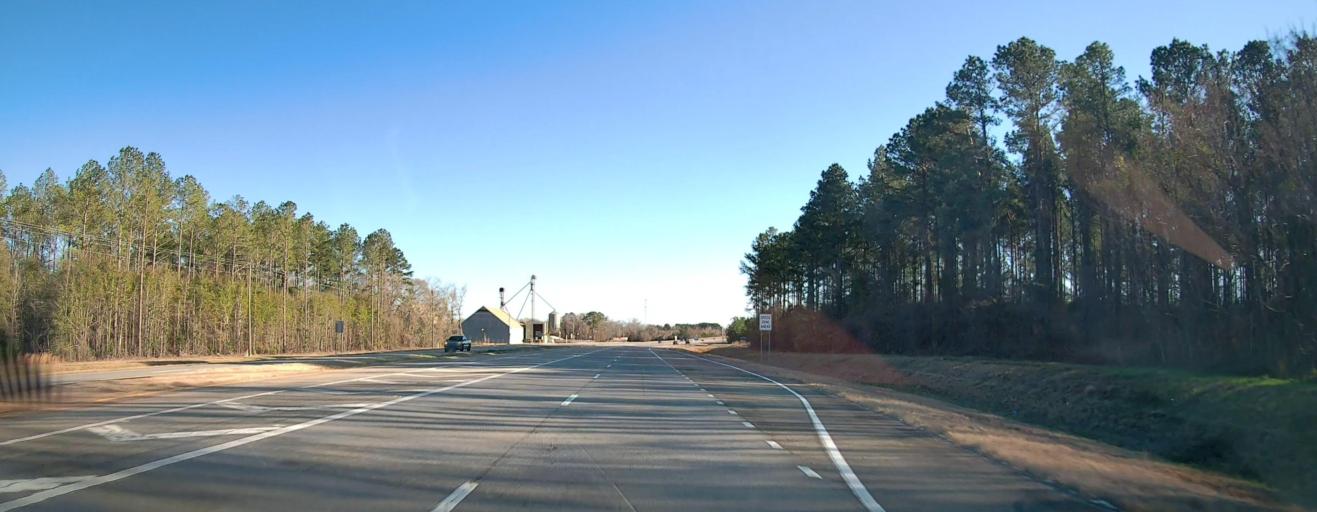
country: US
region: Georgia
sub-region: Sumter County
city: Americus
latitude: 31.9180
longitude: -84.2619
